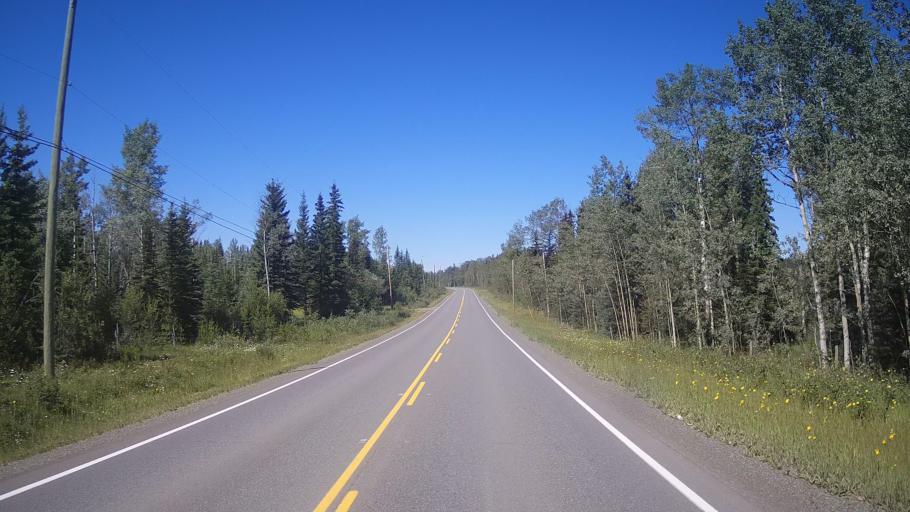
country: CA
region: British Columbia
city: Cache Creek
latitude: 51.5454
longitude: -120.9360
